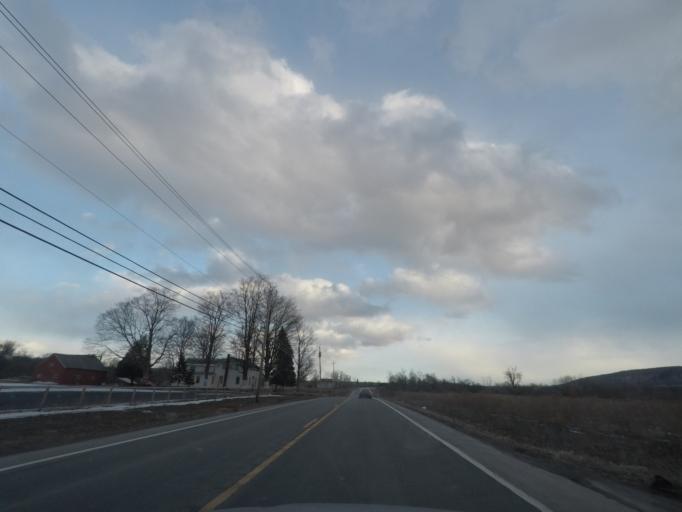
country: US
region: New York
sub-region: Herkimer County
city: Frankfort
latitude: 43.0890
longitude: -75.1287
